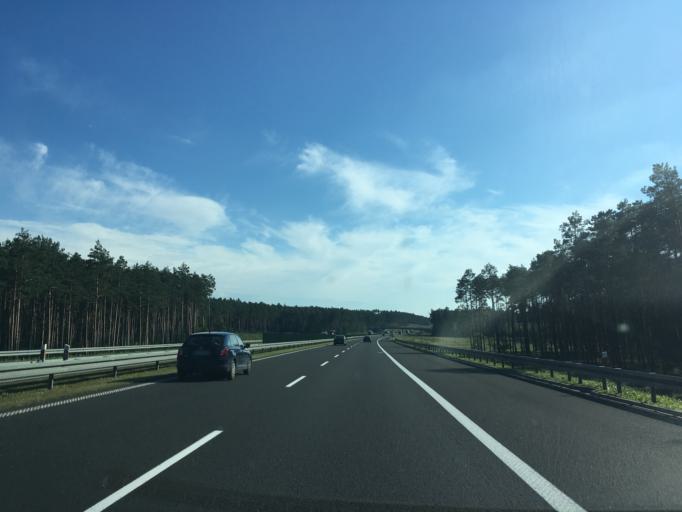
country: PL
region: Kujawsko-Pomorskie
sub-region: Powiat swiecki
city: Warlubie
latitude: 53.5007
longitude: 18.6123
